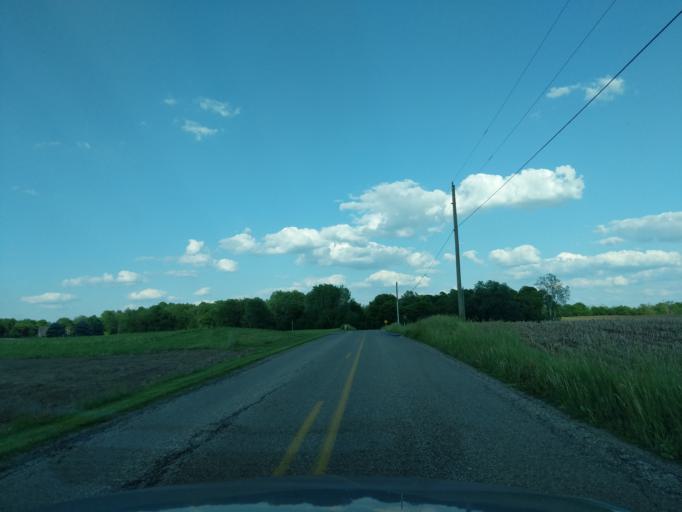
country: US
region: Indiana
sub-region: Whitley County
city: Tri-Lakes
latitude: 41.3026
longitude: -85.5569
